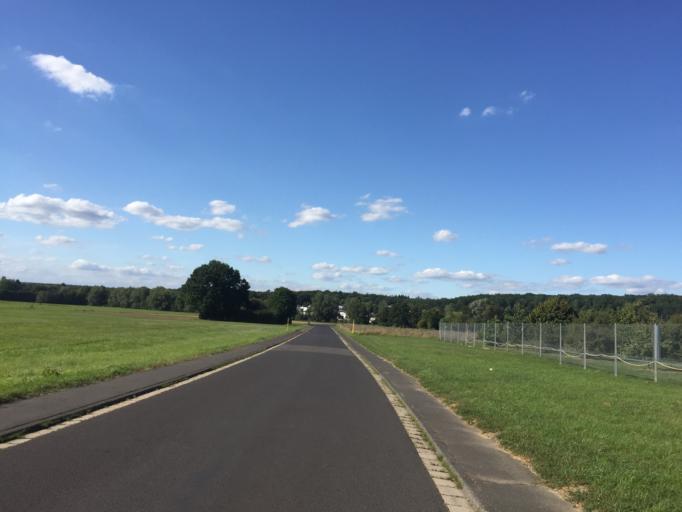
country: DE
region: Hesse
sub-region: Regierungsbezirk Giessen
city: Langgons
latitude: 50.5324
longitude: 8.6842
